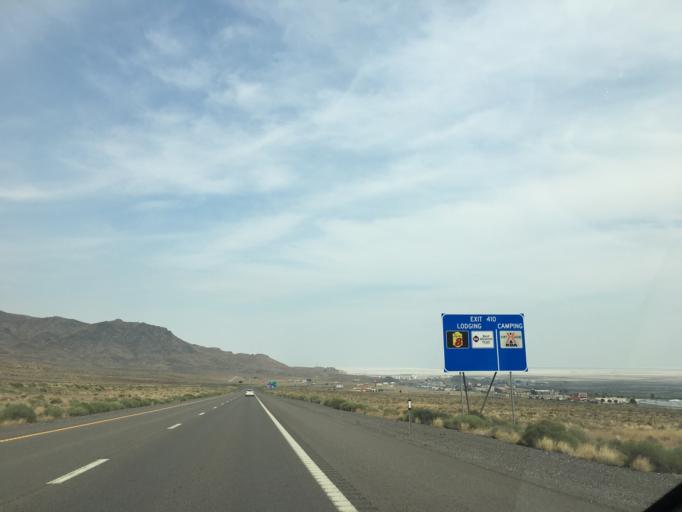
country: US
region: Nevada
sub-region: Elko County
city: West Wendover
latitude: 40.7442
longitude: -114.0864
